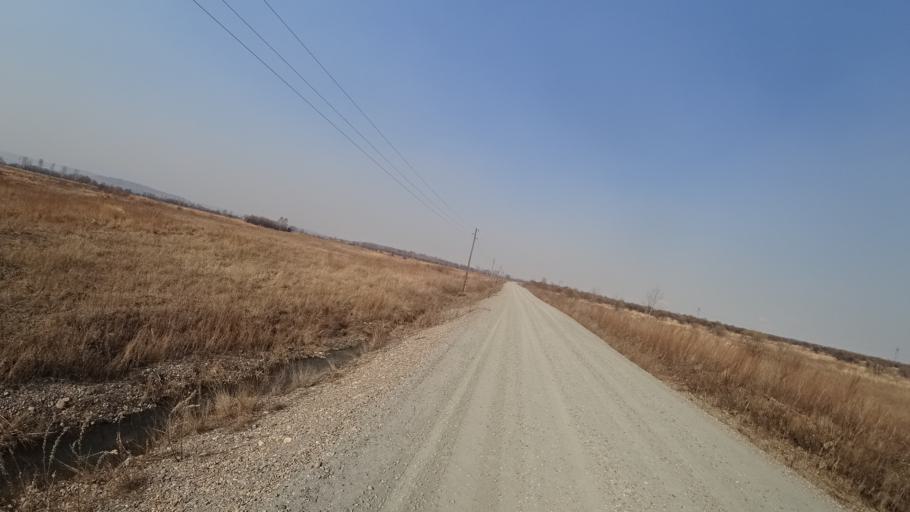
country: RU
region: Amur
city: Novobureyskiy
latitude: 49.8068
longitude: 129.9652
